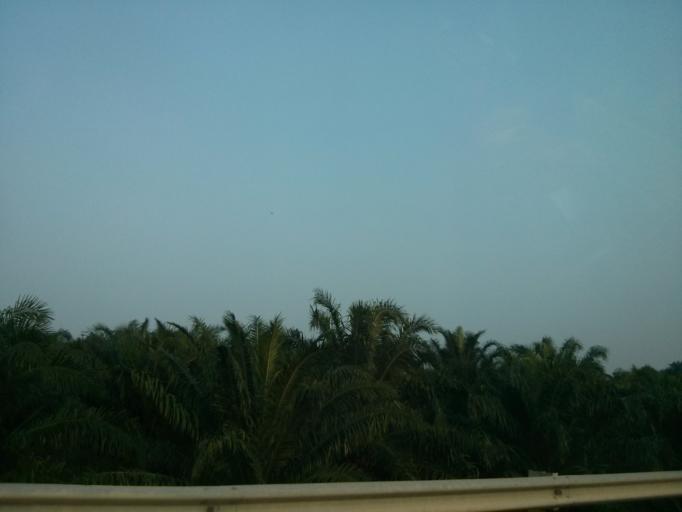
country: MY
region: Putrajaya
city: Putrajaya
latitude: 2.8437
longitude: 101.6944
